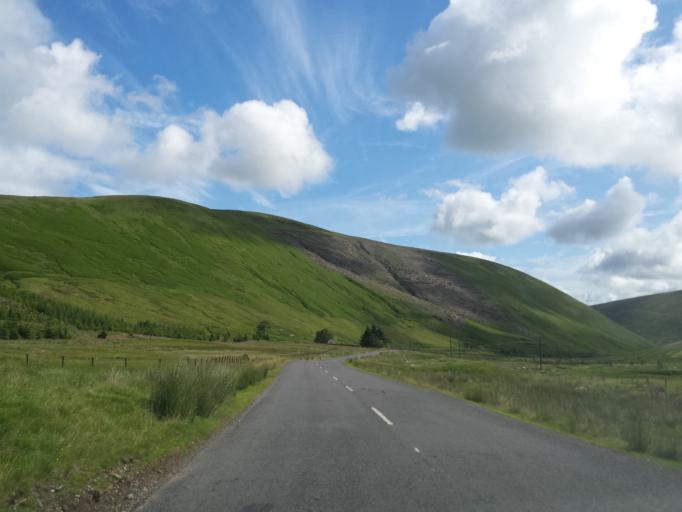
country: GB
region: Scotland
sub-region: Dumfries and Galloway
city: Moffat
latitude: 55.4366
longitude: -3.2569
